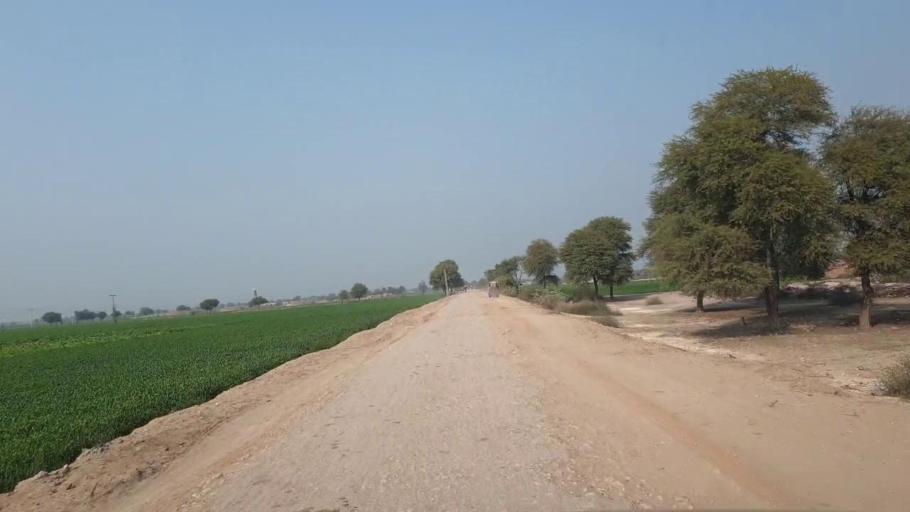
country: PK
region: Sindh
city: Hala
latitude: 25.8587
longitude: 68.4619
